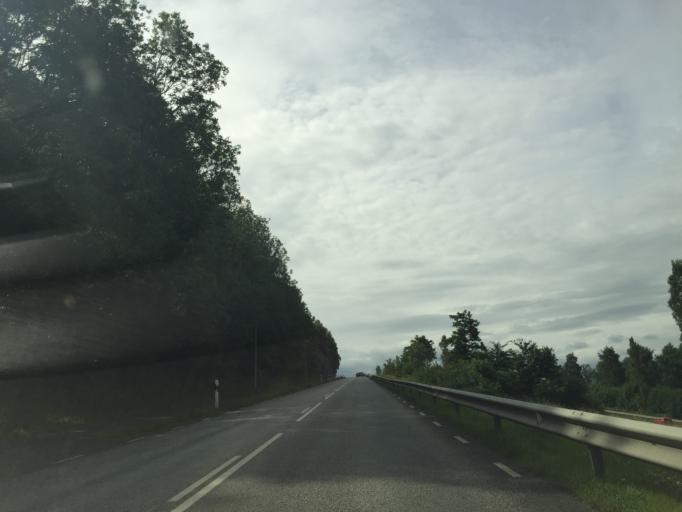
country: SE
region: Joenkoeping
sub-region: Jonkopings Kommun
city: Kaxholmen
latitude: 57.8298
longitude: 14.2710
